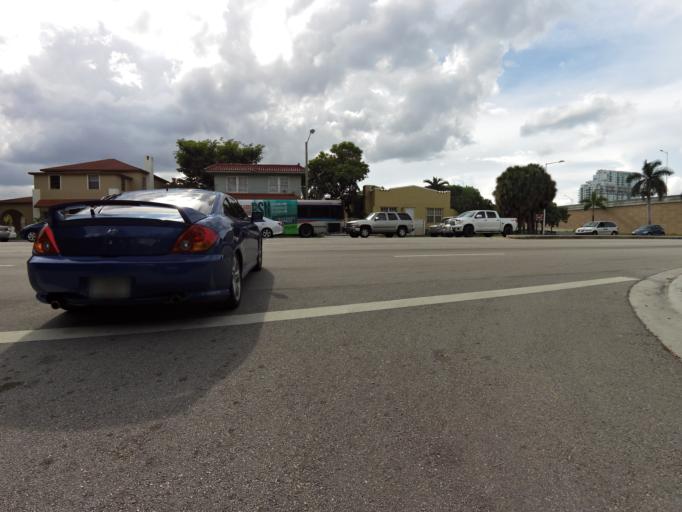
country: US
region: Florida
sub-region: Miami-Dade County
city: Miami
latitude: 25.7816
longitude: -80.2224
